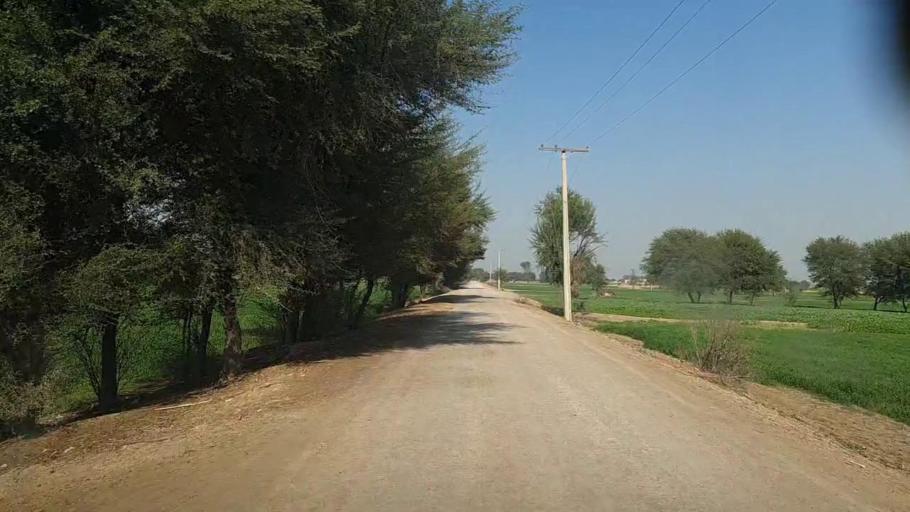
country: PK
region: Sindh
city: Khairpur
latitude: 27.9983
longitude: 69.8497
